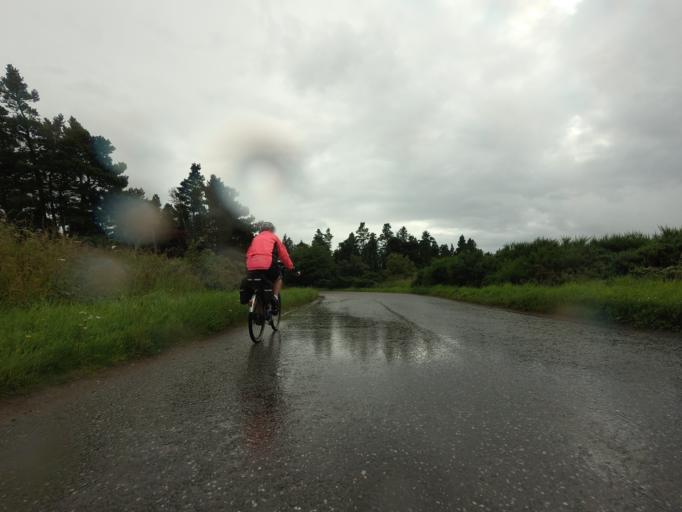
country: GB
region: Scotland
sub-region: Moray
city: Fochabers
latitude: 57.6562
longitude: -3.0573
